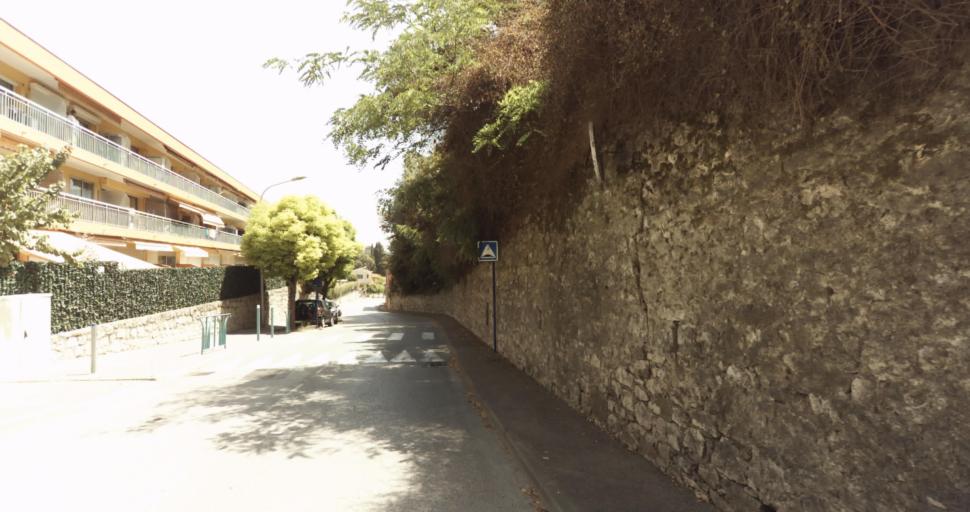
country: FR
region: Provence-Alpes-Cote d'Azur
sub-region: Departement des Alpes-Maritimes
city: Roquebrune-Cap-Martin
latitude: 43.7773
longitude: 7.4724
